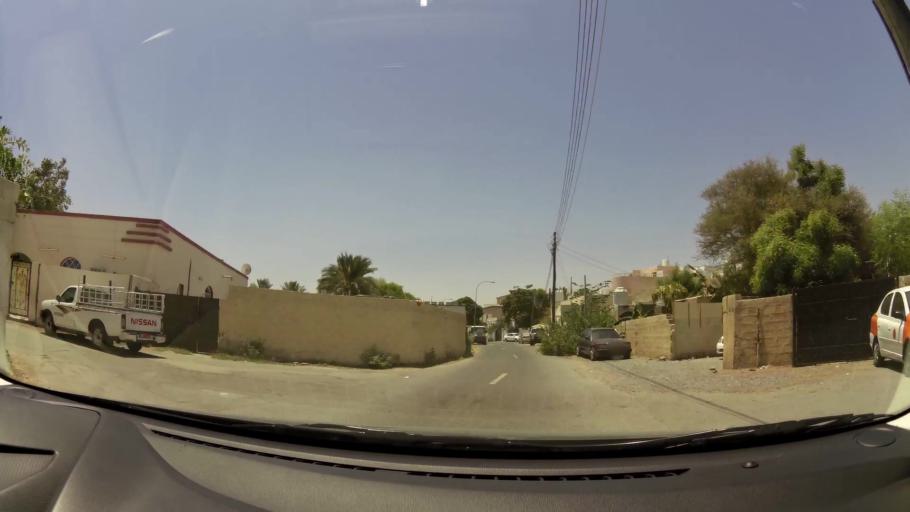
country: OM
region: Muhafazat Masqat
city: As Sib al Jadidah
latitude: 23.6248
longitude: 58.2422
